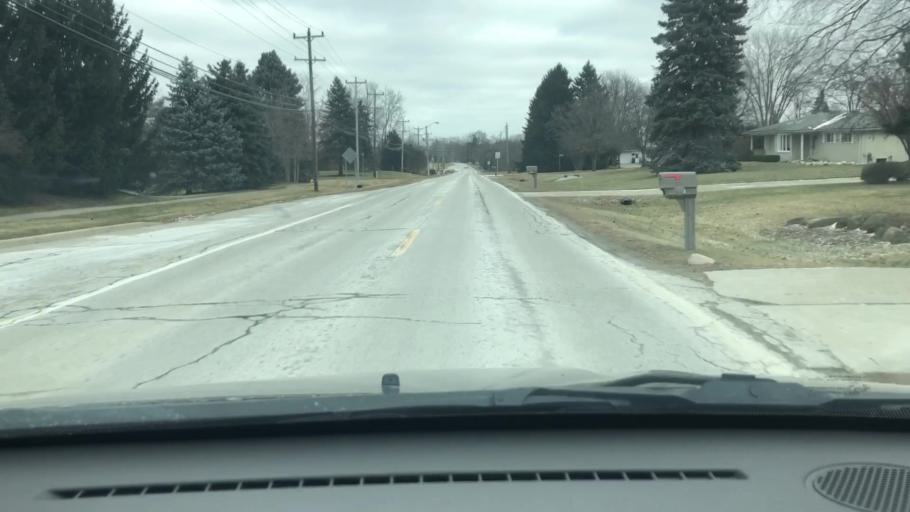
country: US
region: Michigan
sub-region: Macomb County
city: Shelby
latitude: 42.7235
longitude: -83.0538
